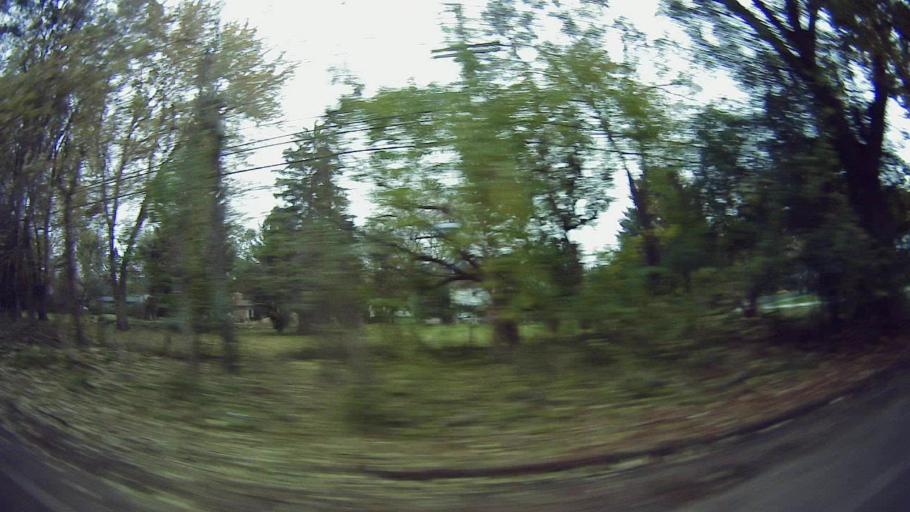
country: US
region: Michigan
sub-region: Oakland County
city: Franklin
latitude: 42.5152
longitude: -83.3021
